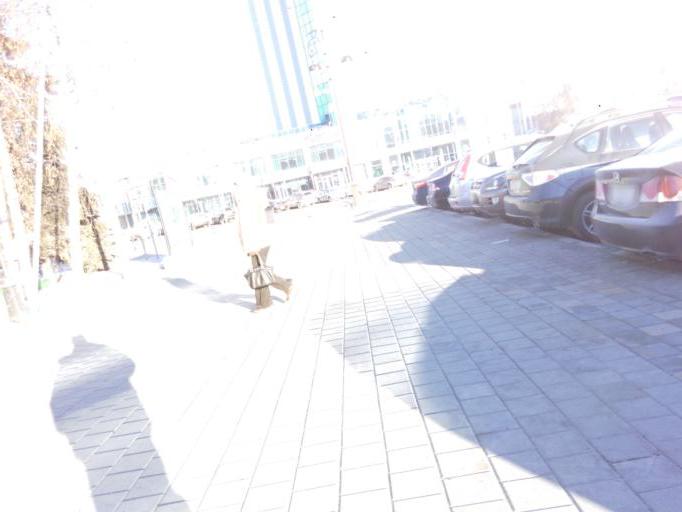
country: RU
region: Tjumen
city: Tyumen
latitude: 57.1389
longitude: 65.5669
